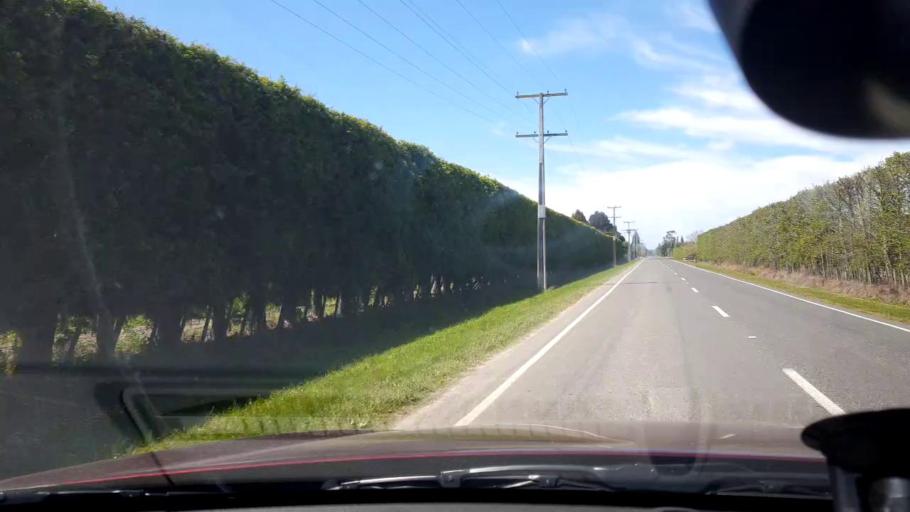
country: NZ
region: Gisborne
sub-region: Gisborne District
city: Gisborne
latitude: -38.6388
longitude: 177.9326
